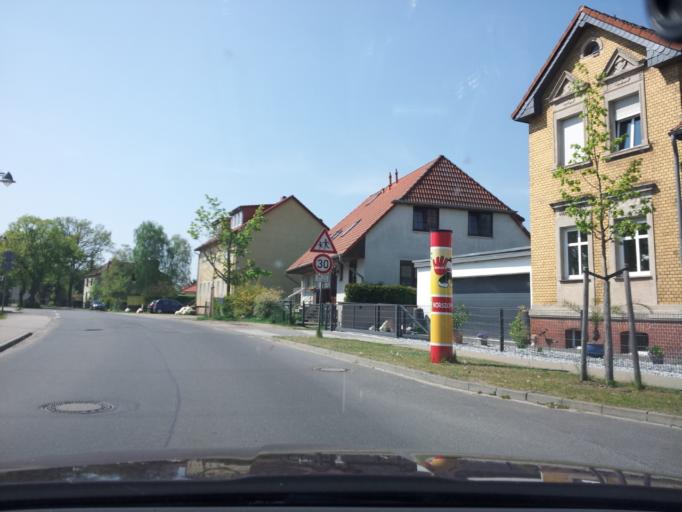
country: DE
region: Brandenburg
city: Michendorf
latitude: 52.3178
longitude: 13.1259
